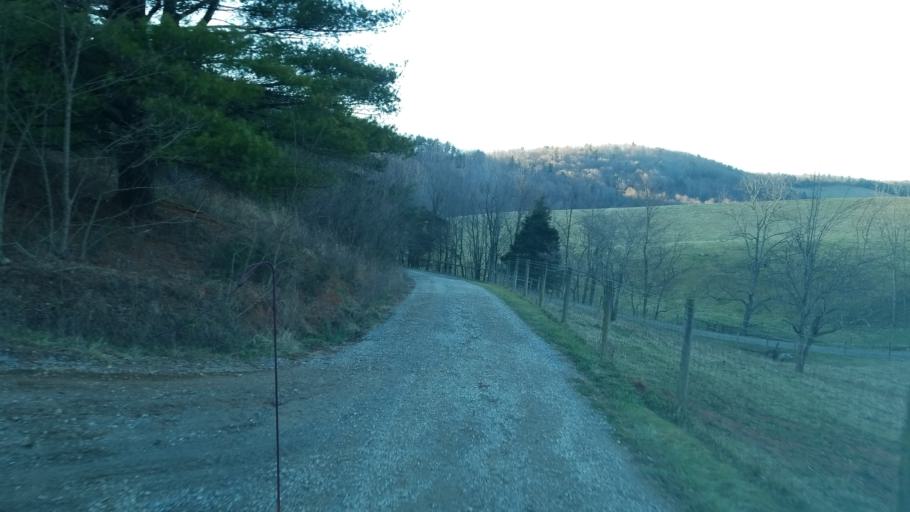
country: US
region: Virginia
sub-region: Giles County
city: Narrows
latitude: 37.1918
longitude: -80.8465
